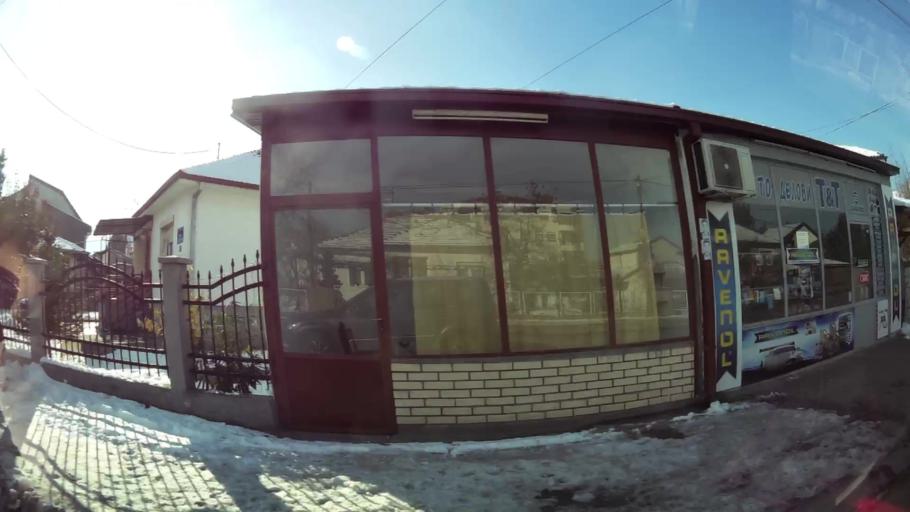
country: MK
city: Krushopek
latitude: 42.0053
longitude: 21.3671
